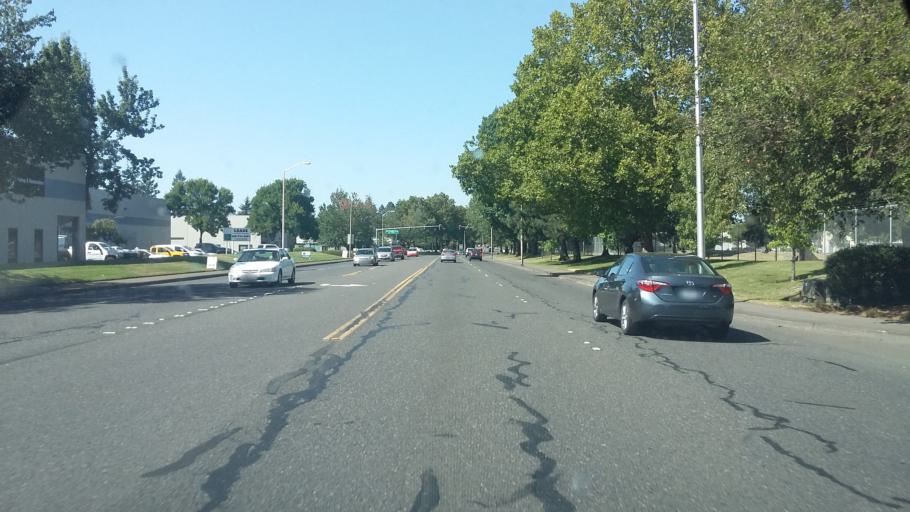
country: US
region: Washington
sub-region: Clark County
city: Orchards
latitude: 45.6486
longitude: -122.5583
